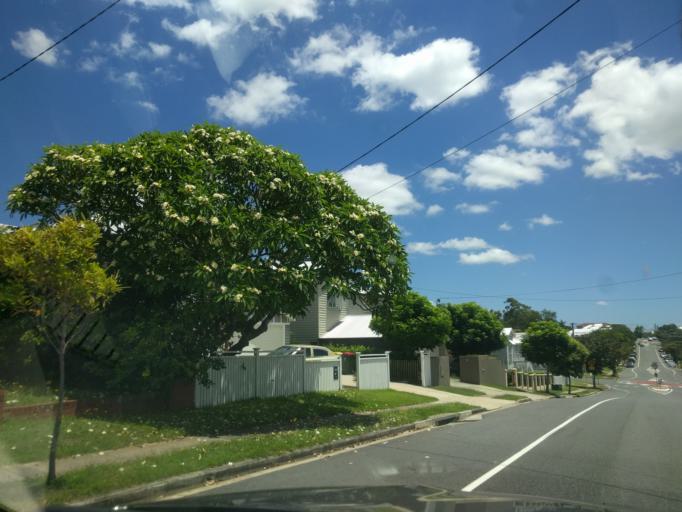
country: AU
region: Queensland
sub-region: Brisbane
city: Gordon Park
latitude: -27.4157
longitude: 153.0267
